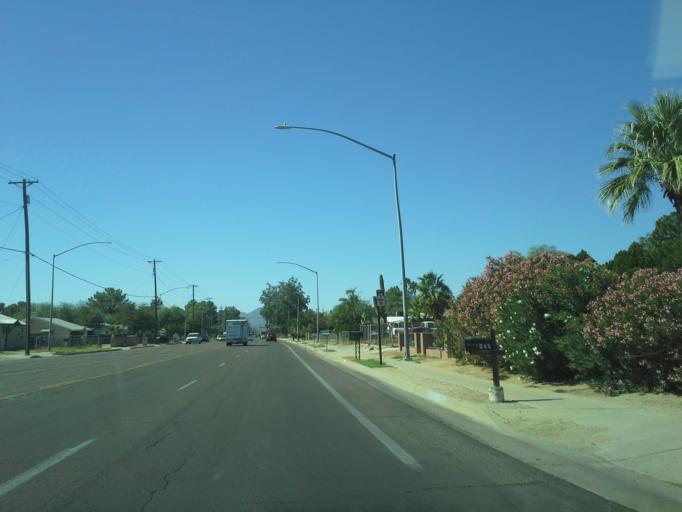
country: US
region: Arizona
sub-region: Pima County
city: Catalina Foothills
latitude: 32.2721
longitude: -110.9566
